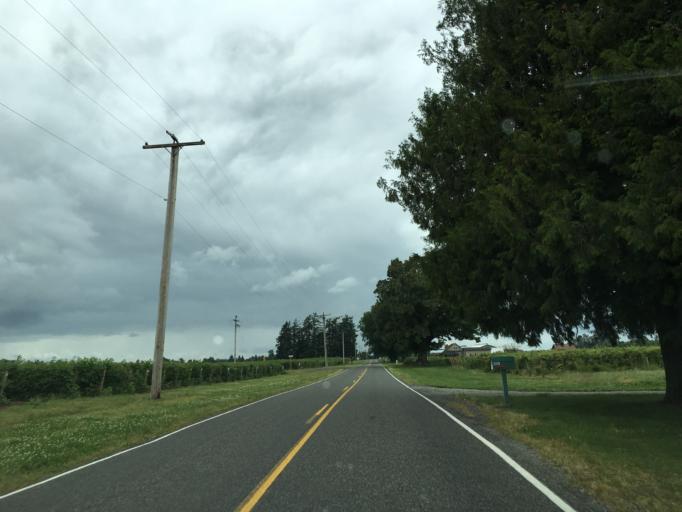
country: US
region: Washington
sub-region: Whatcom County
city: Everson
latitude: 48.9820
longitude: -122.3644
